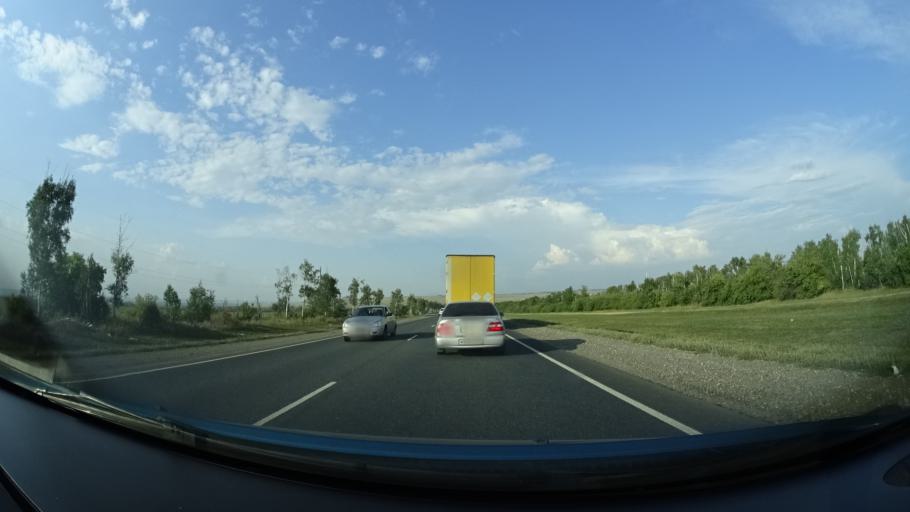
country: RU
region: Samara
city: Krasnyy Yar
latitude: 53.6753
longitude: 50.7722
